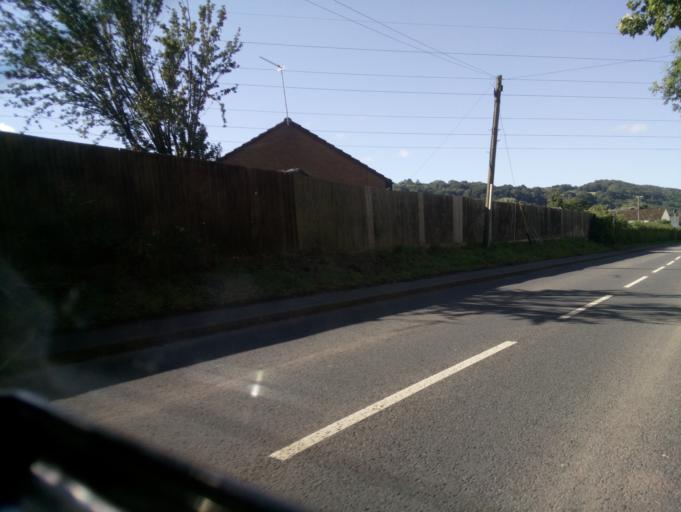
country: GB
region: England
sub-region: Herefordshire
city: Walford
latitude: 51.8879
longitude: -2.5910
